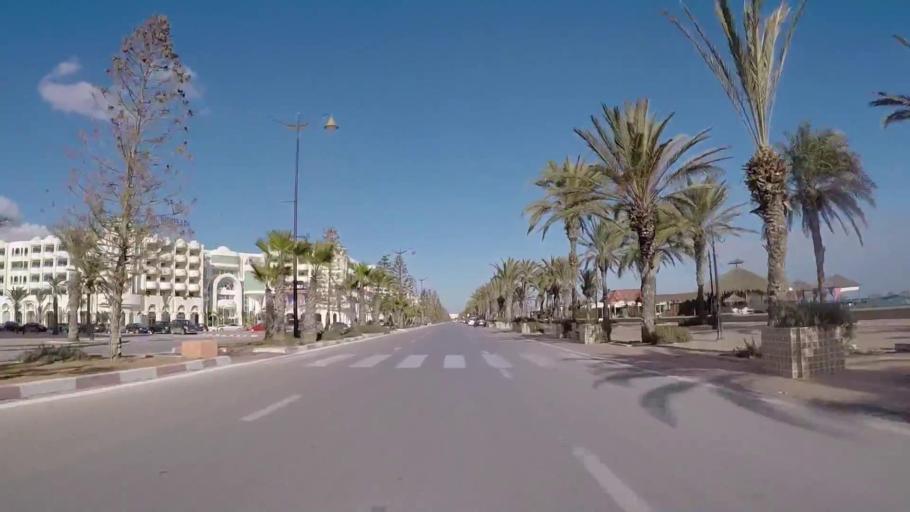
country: TN
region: Nabul
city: Al Hammamat
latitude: 36.3651
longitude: 10.5372
